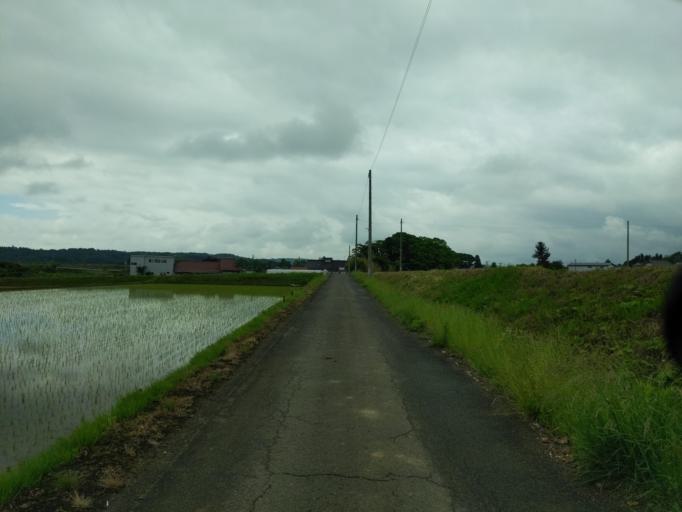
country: JP
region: Fukushima
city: Koriyama
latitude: 37.3517
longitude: 140.2785
